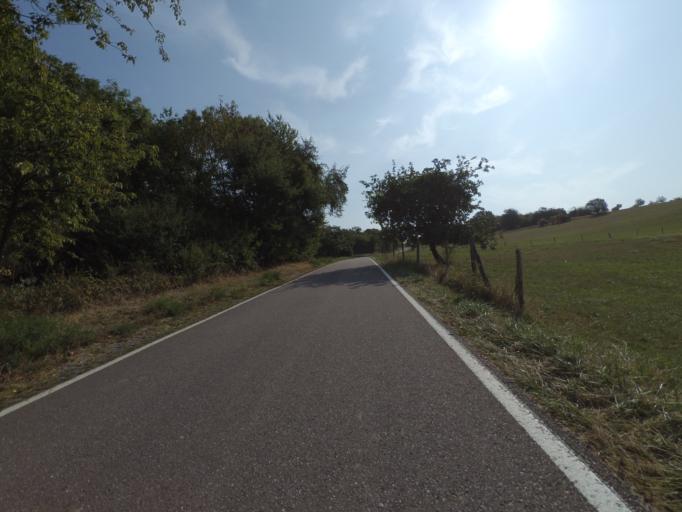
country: DE
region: Saarland
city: Perl
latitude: 49.5127
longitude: 6.4204
